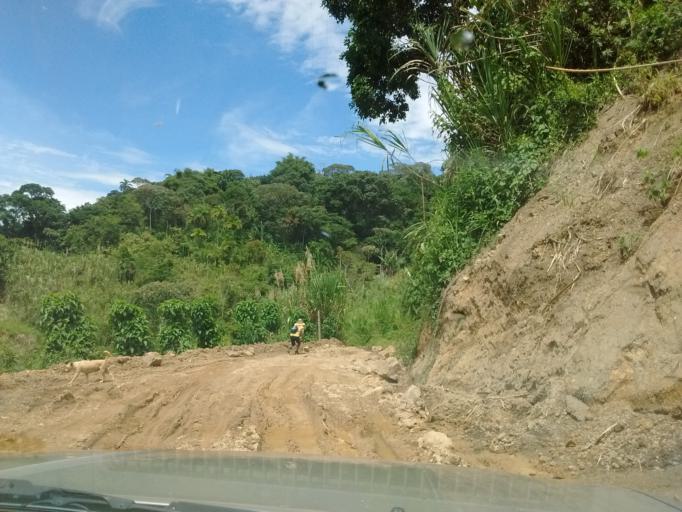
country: CO
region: Cauca
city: Morales
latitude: 2.6738
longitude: -76.7638
